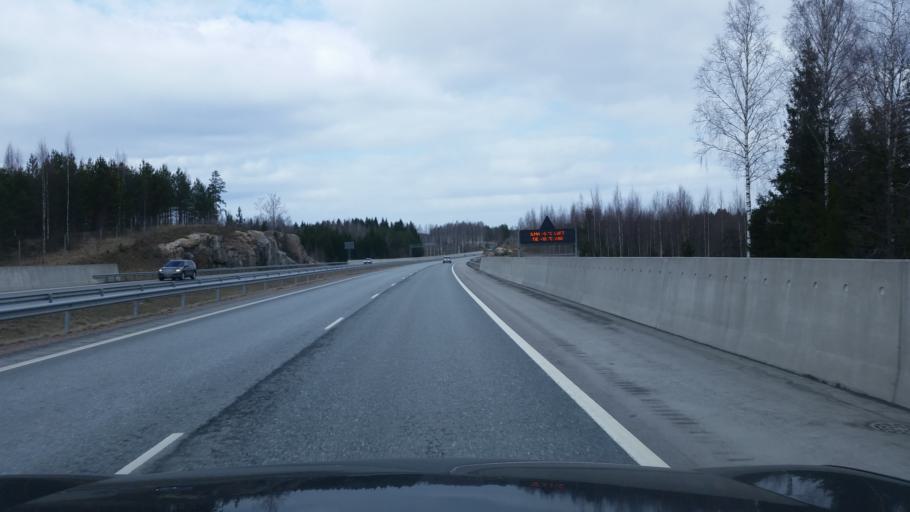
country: FI
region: Uusimaa
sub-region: Helsinki
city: Sammatti
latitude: 60.3489
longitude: 23.8997
